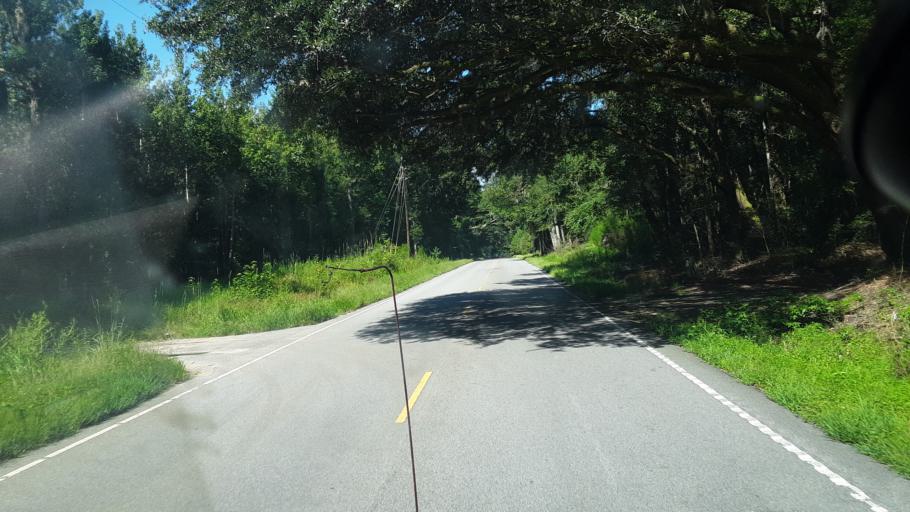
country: US
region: South Carolina
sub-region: Jasper County
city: Ridgeland
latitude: 32.5894
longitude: -80.9449
